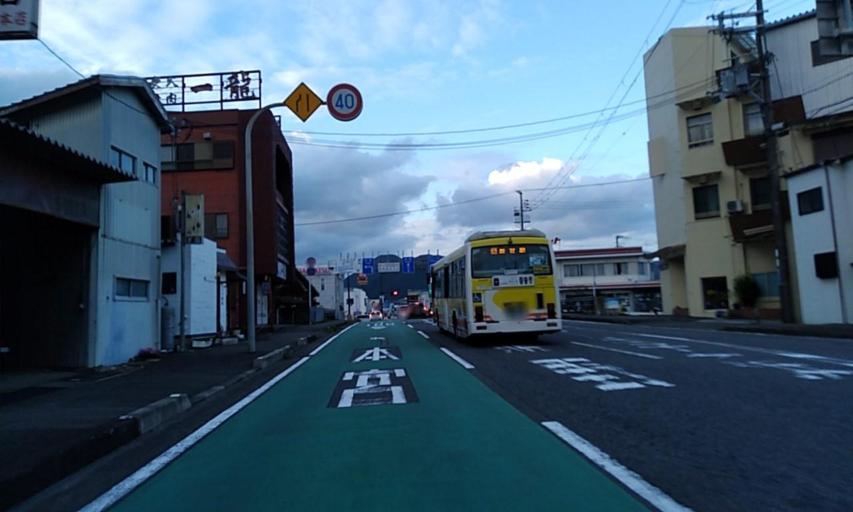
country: JP
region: Wakayama
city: Shingu
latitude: 33.7181
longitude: 135.9871
